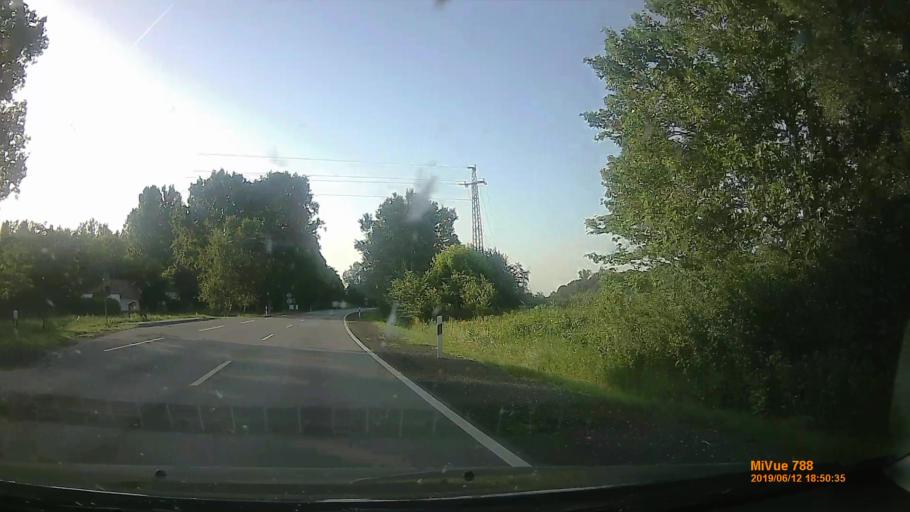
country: HU
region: Bacs-Kiskun
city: Kiskunfelegyhaza
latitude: 46.6489
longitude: 19.8756
